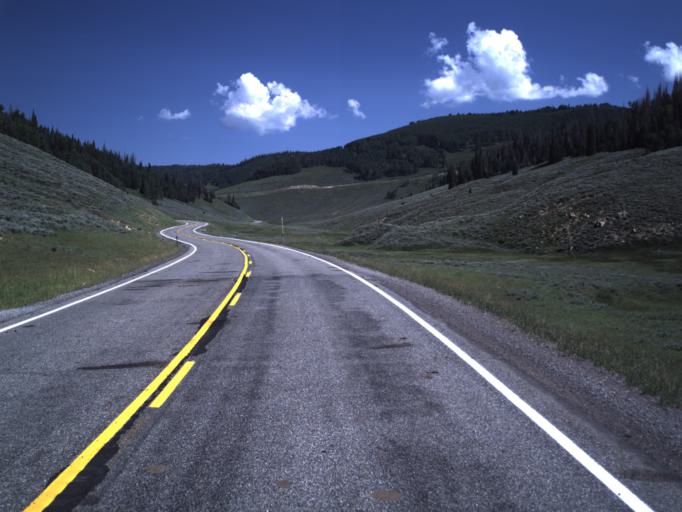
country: US
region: Utah
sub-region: Sanpete County
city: Fairview
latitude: 39.6673
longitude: -111.2441
